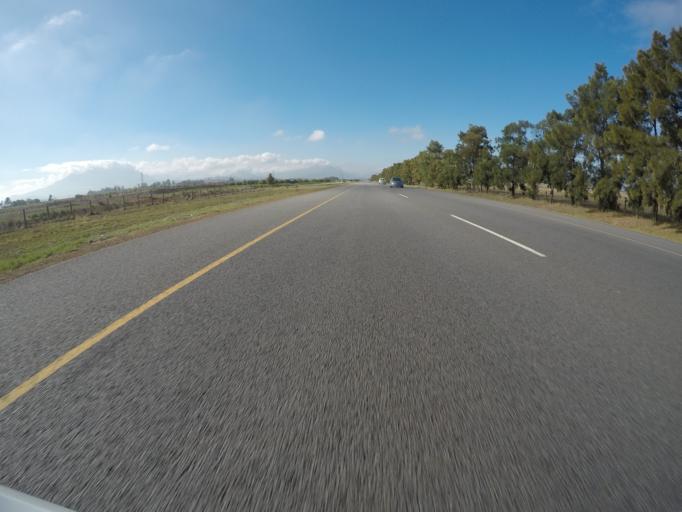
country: ZA
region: Western Cape
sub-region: City of Cape Town
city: Kraaifontein
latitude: -33.8436
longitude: 18.8017
